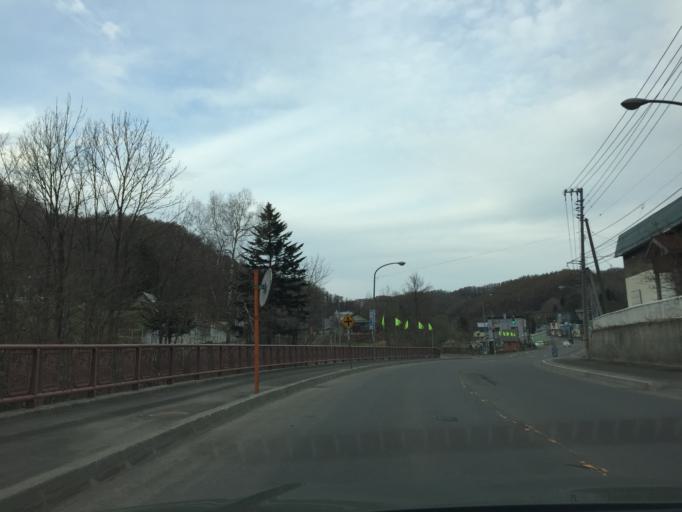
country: JP
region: Hokkaido
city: Utashinai
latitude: 43.5068
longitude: 142.0209
